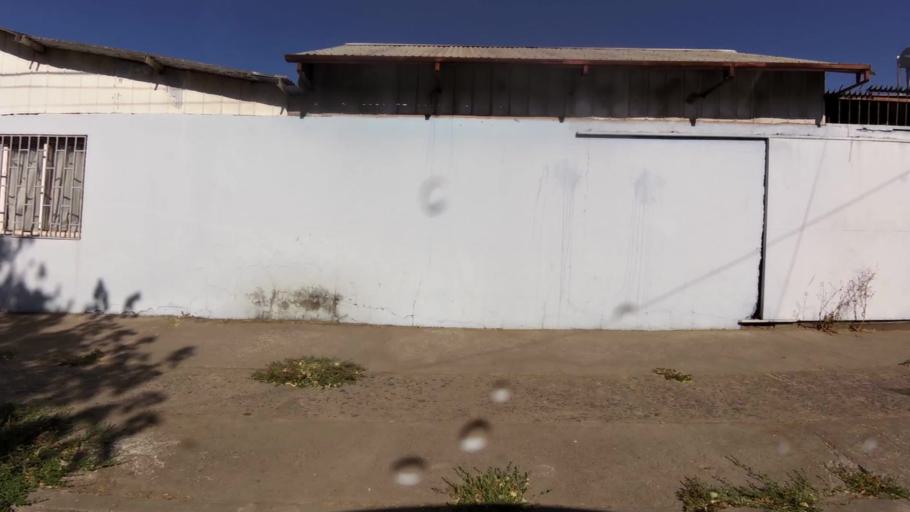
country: CL
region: Maule
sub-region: Provincia de Talca
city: Talca
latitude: -35.4439
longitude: -71.6591
